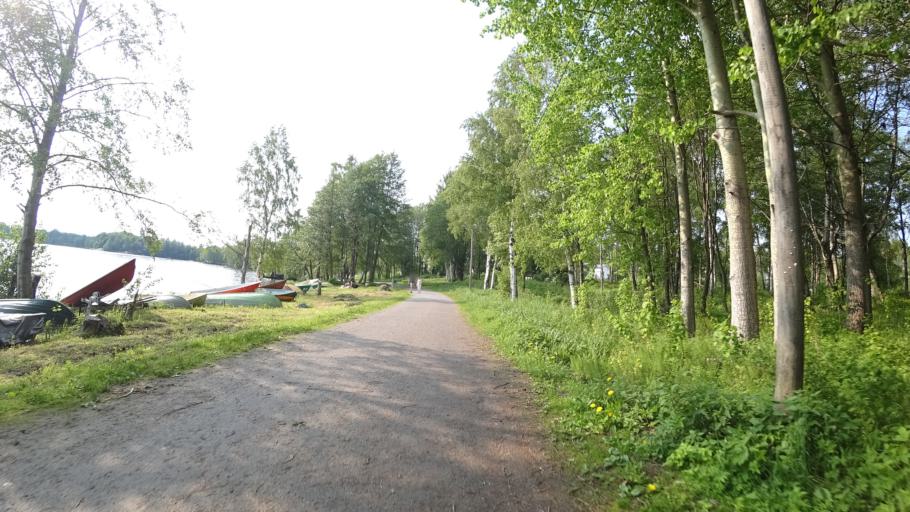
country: FI
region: Pirkanmaa
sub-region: Tampere
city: Tampere
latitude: 61.5021
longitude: 23.7053
